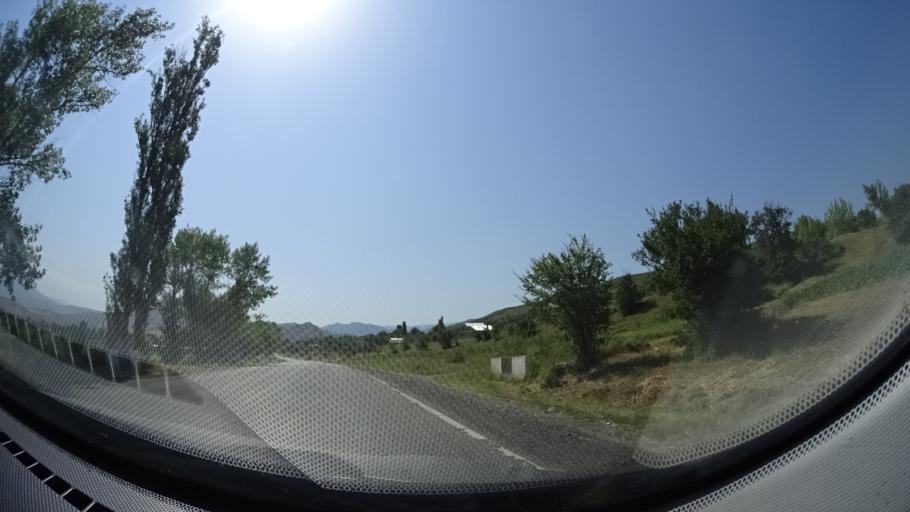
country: GE
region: Samtskhe-Javakheti
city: Akhaltsikhe
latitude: 41.6402
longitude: 43.0295
